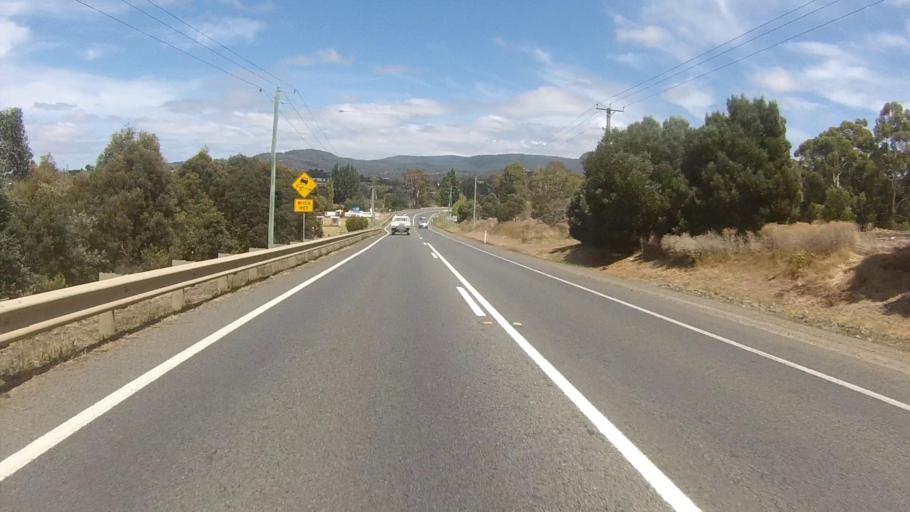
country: AU
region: Tasmania
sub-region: Kingborough
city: Margate
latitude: -43.0197
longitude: 147.2682
